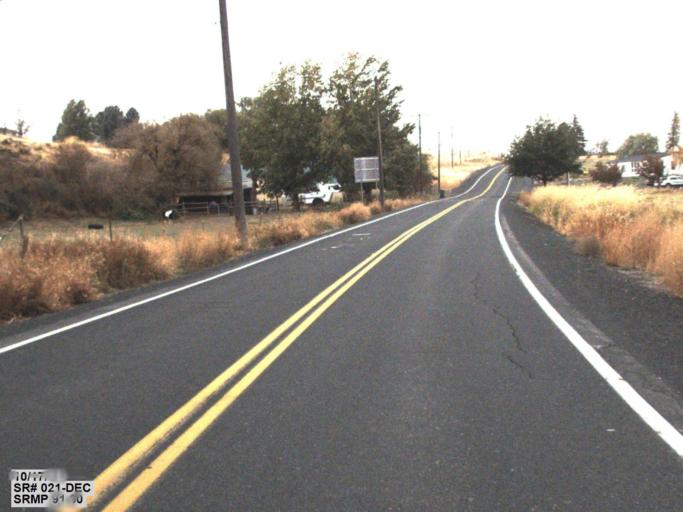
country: US
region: Washington
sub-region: Okanogan County
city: Coulee Dam
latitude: 47.7578
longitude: -118.7114
